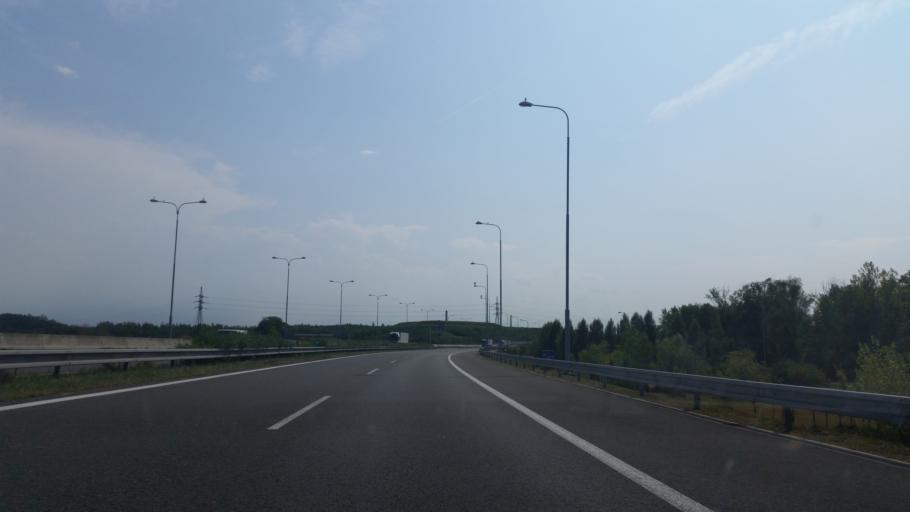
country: PL
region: Silesian Voivodeship
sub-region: Powiat raciborski
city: Chalupki
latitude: 49.8824
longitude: 18.3058
